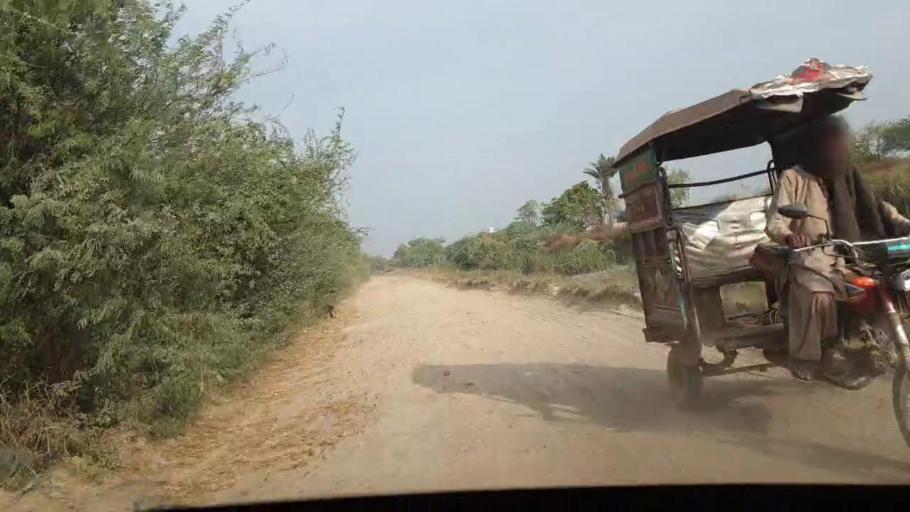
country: PK
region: Sindh
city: Chuhar Jamali
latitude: 24.3939
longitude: 67.9740
